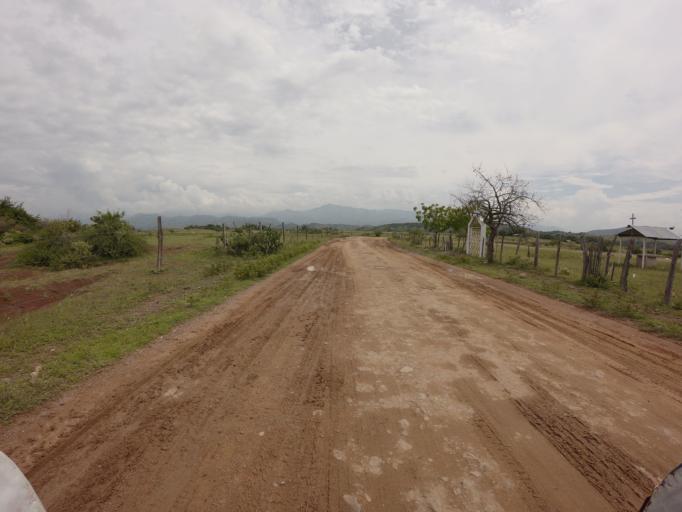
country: CO
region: Tolima
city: Natagaima
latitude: 3.4655
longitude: -75.1428
